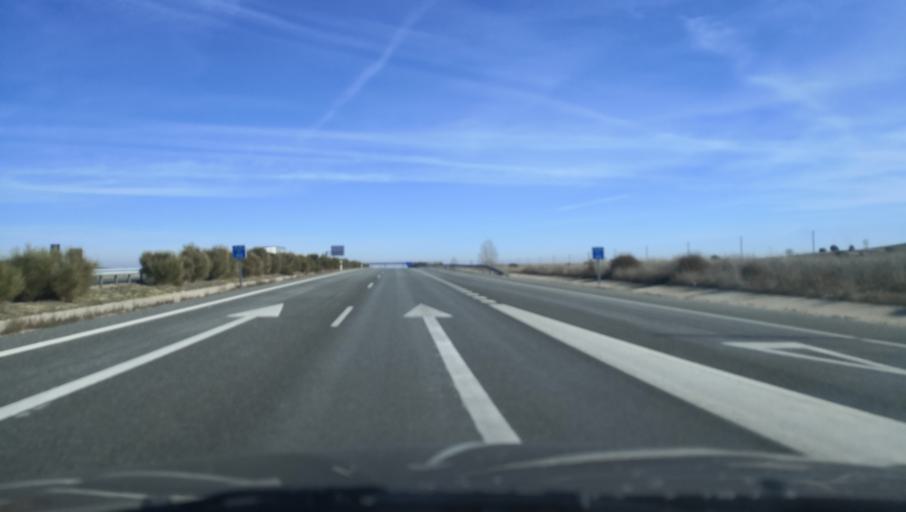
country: ES
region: Castille and Leon
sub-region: Provincia de Avila
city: Narros del Castillo
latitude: 40.8780
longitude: -5.0528
